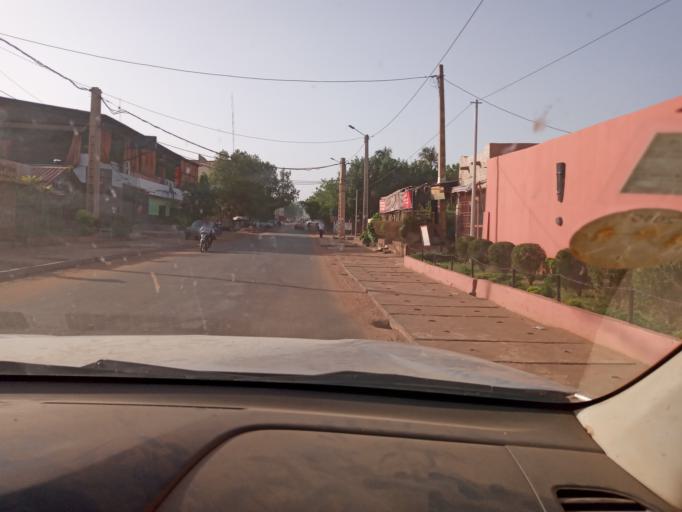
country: ML
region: Bamako
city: Bamako
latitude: 12.6595
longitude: -7.9718
